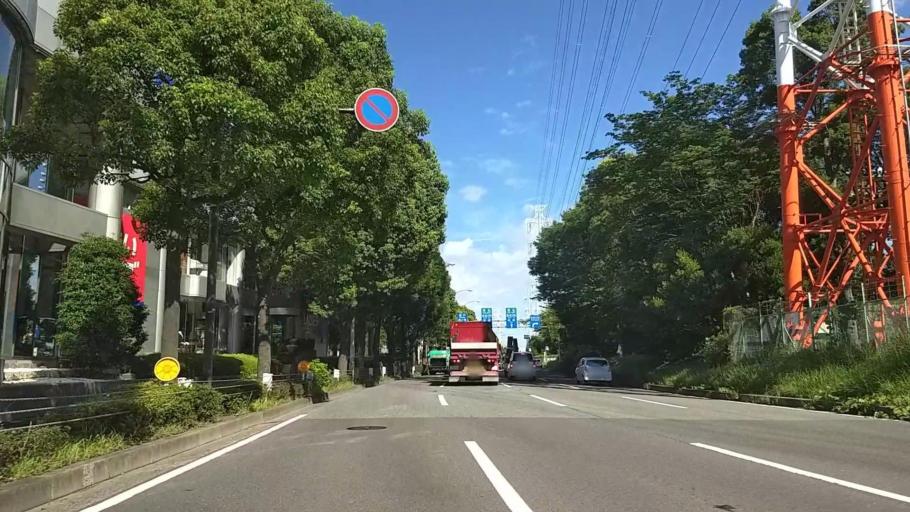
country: JP
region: Tokyo
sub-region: Machida-shi
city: Machida
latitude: 35.5380
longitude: 139.5638
